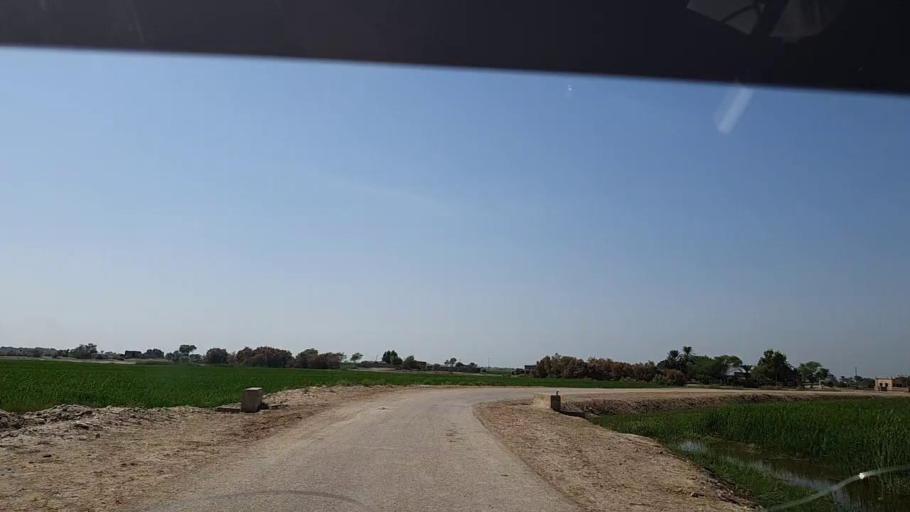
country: PK
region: Sindh
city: Tangwani
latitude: 28.3156
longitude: 69.0951
